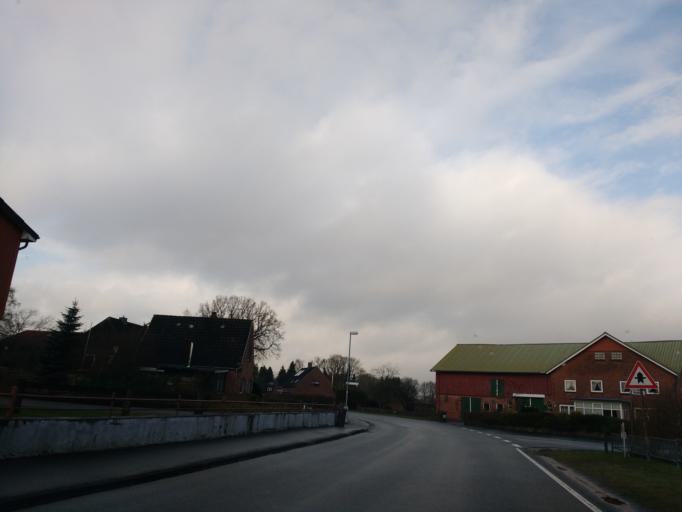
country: DE
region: Schleswig-Holstein
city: Luhnstedt
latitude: 54.2098
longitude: 9.7089
